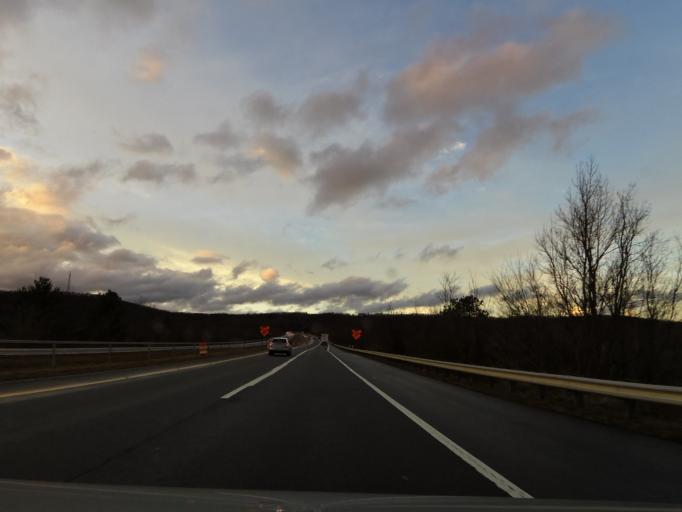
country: US
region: Tennessee
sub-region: Campbell County
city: Jacksboro
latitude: 36.4192
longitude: -84.2845
